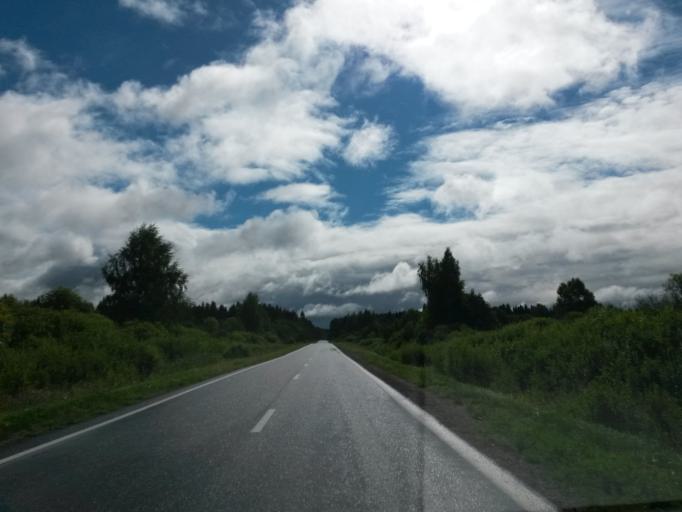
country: RU
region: Jaroslavl
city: Konstantinovskiy
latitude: 57.8300
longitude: 39.6701
